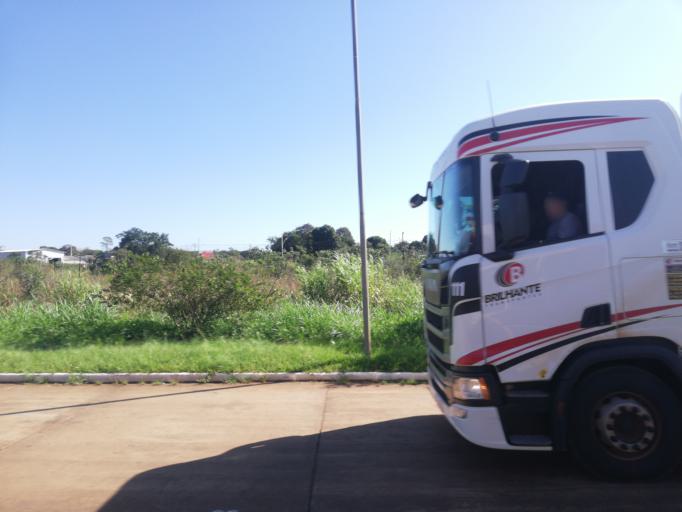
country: AR
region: Misiones
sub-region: Departamento de Iguazu
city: Puerto Iguazu
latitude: -25.5779
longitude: -54.5570
